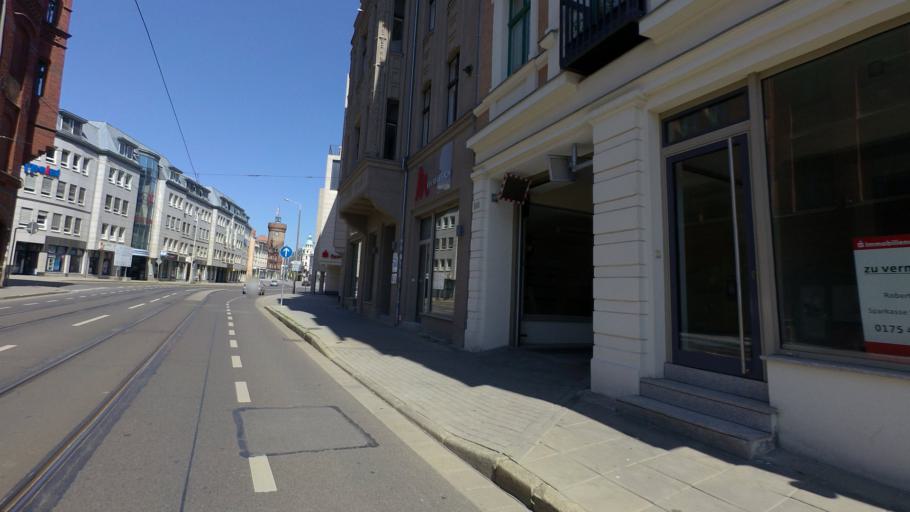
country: DE
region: Brandenburg
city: Cottbus
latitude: 51.7558
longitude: 14.3331
